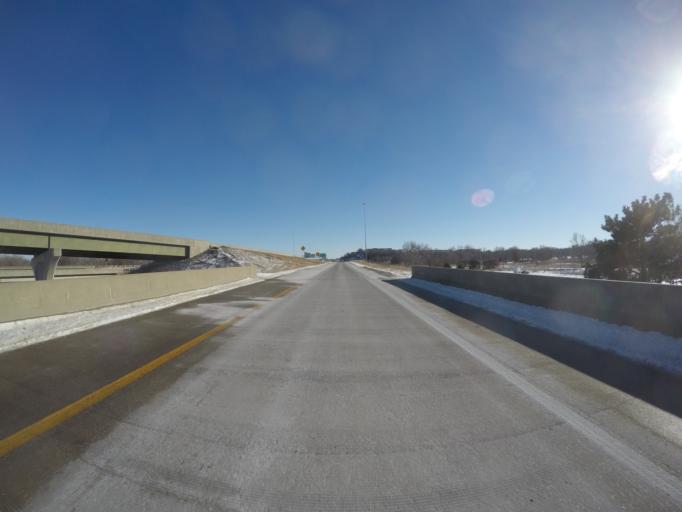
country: US
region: Kansas
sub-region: Shawnee County
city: Topeka
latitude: 39.0506
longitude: -95.7731
